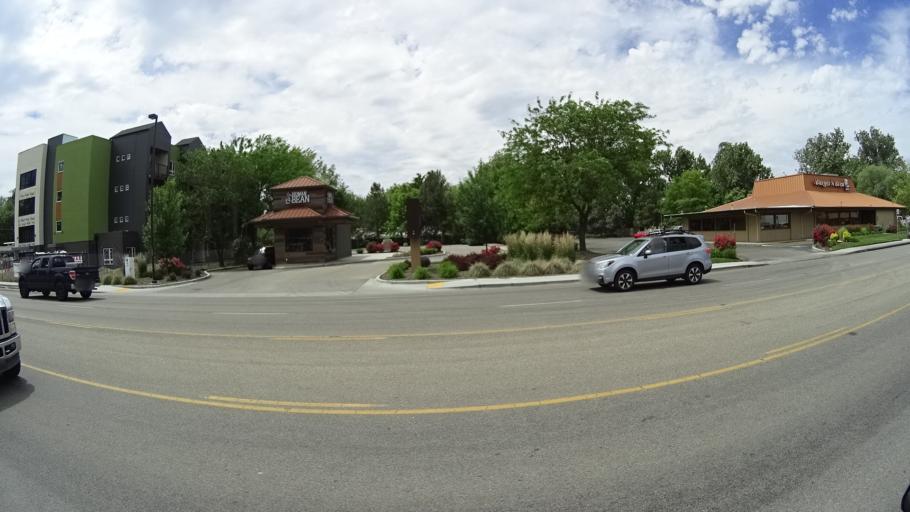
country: US
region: Idaho
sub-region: Ada County
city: Garden City
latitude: 43.6446
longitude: -116.2420
